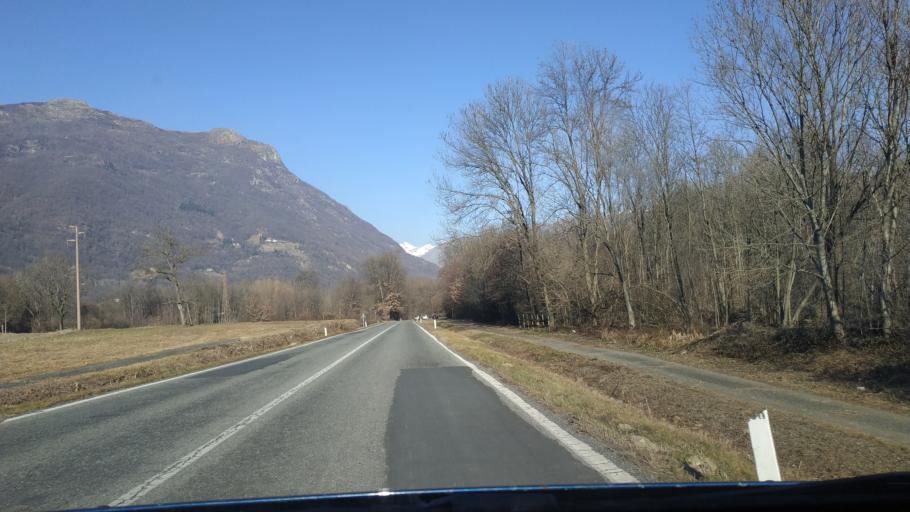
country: IT
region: Piedmont
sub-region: Provincia di Torino
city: Lessolo
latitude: 45.4869
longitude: 7.8288
